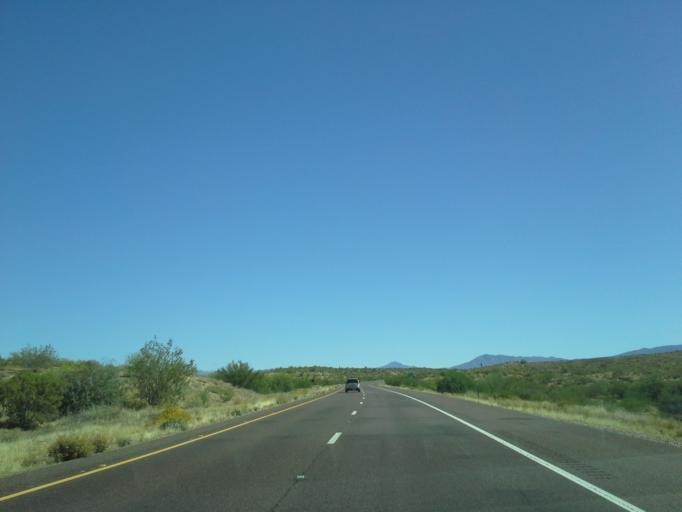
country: US
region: Arizona
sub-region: Maricopa County
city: Fountain Hills
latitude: 33.6140
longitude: -111.5717
